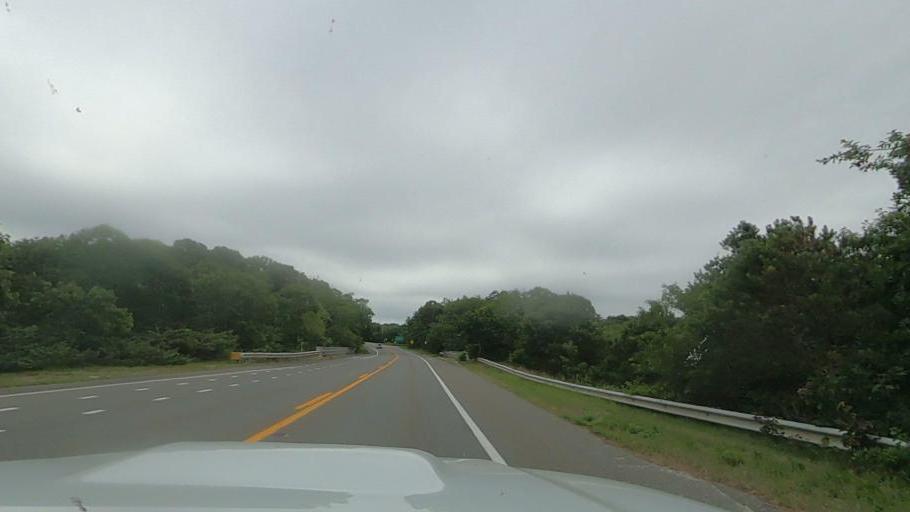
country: US
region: Massachusetts
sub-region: Barnstable County
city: Truro
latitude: 41.9938
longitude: -70.0485
